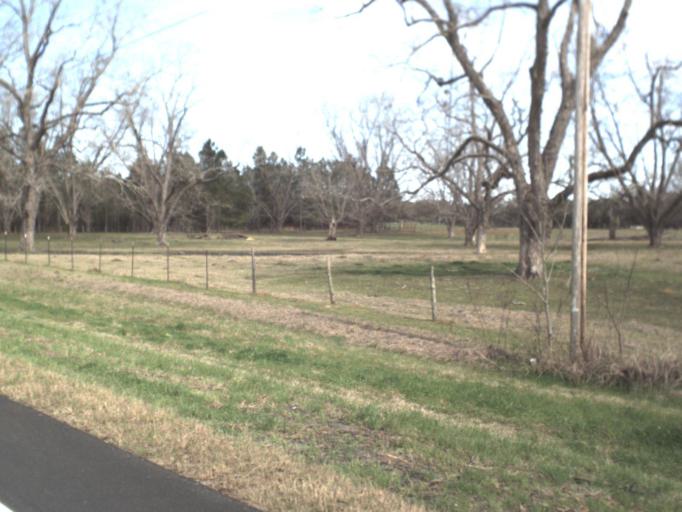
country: US
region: Florida
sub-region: Washington County
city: Chipley
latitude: 30.6795
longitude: -85.3936
